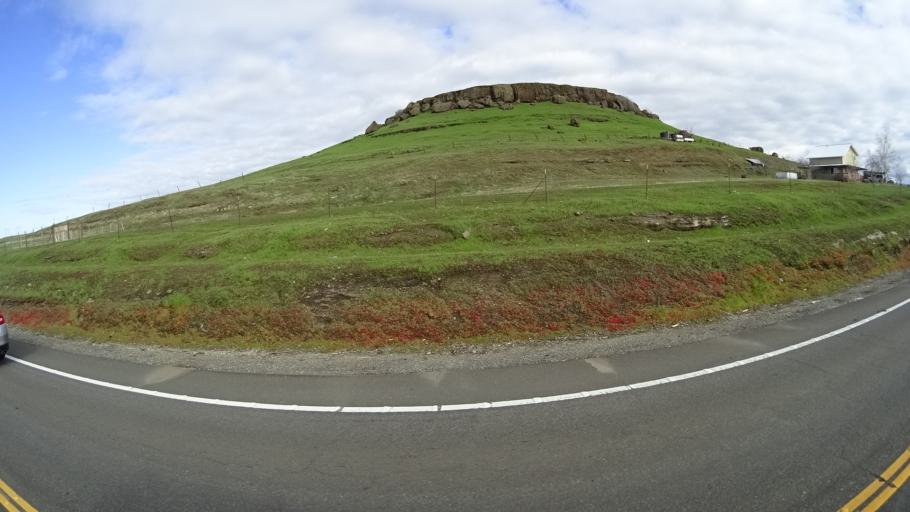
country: US
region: California
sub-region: Butte County
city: Durham
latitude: 39.6387
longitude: -121.6837
